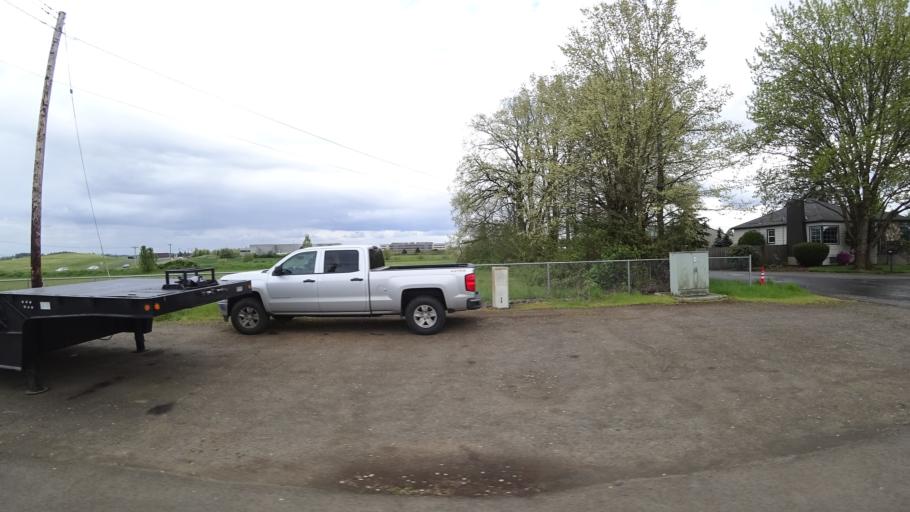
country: US
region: Oregon
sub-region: Washington County
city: Hillsboro
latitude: 45.5500
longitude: -122.9644
